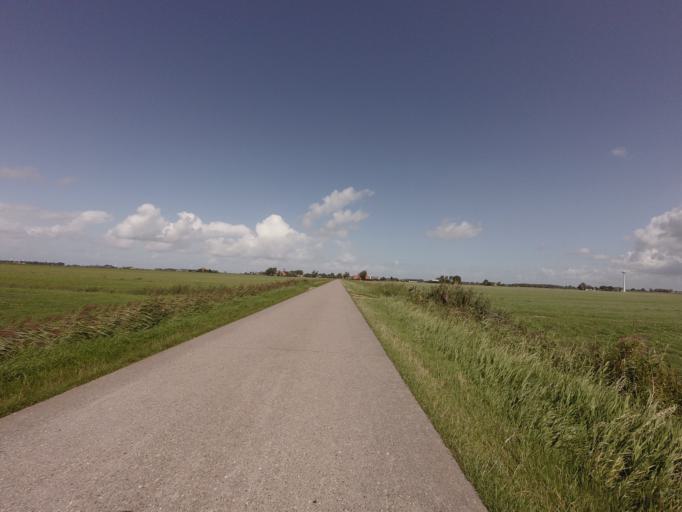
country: NL
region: Friesland
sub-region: Sudwest Fryslan
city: Makkum
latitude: 53.0721
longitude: 5.4538
